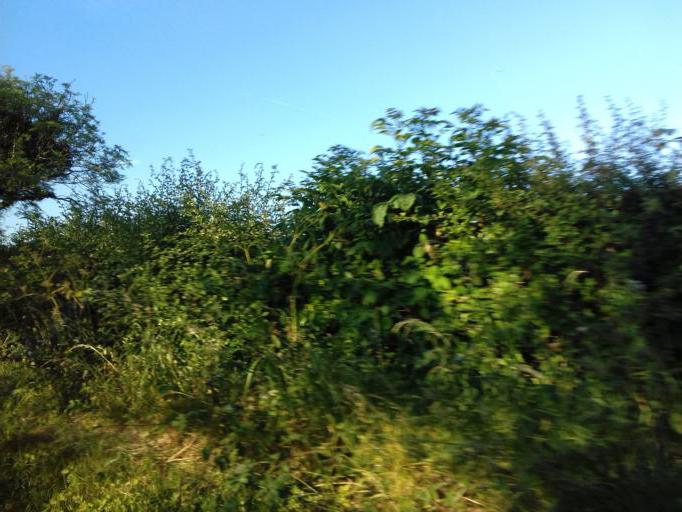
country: IE
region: Leinster
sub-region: An Mhi
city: Ashbourne
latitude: 53.5683
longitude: -6.3516
